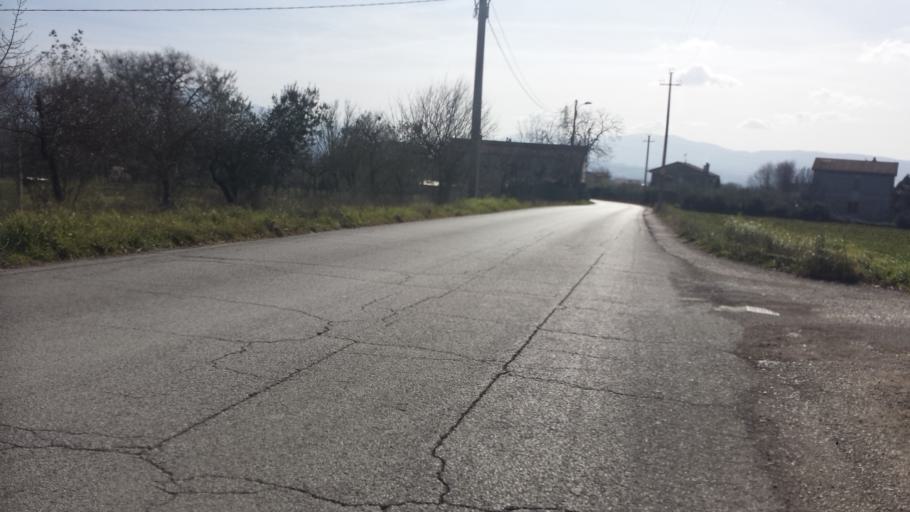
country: IT
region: Umbria
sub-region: Provincia di Terni
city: San Gemini
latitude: 42.5850
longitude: 12.5799
